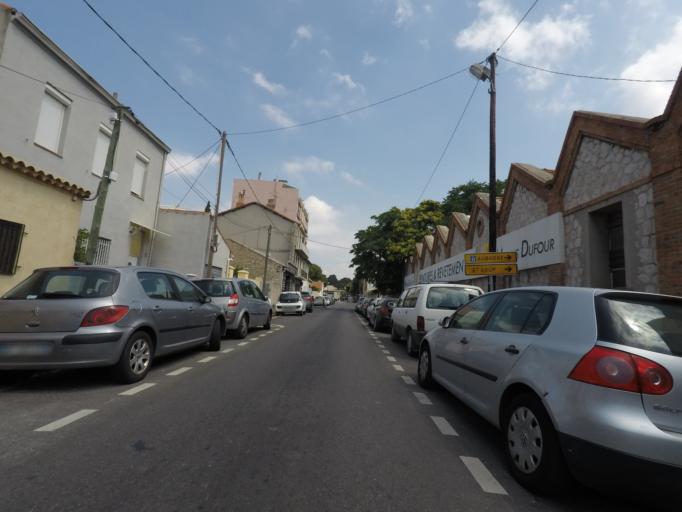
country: FR
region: Provence-Alpes-Cote d'Azur
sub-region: Departement des Bouches-du-Rhone
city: Marseille 10
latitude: 43.2823
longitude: 5.4127
